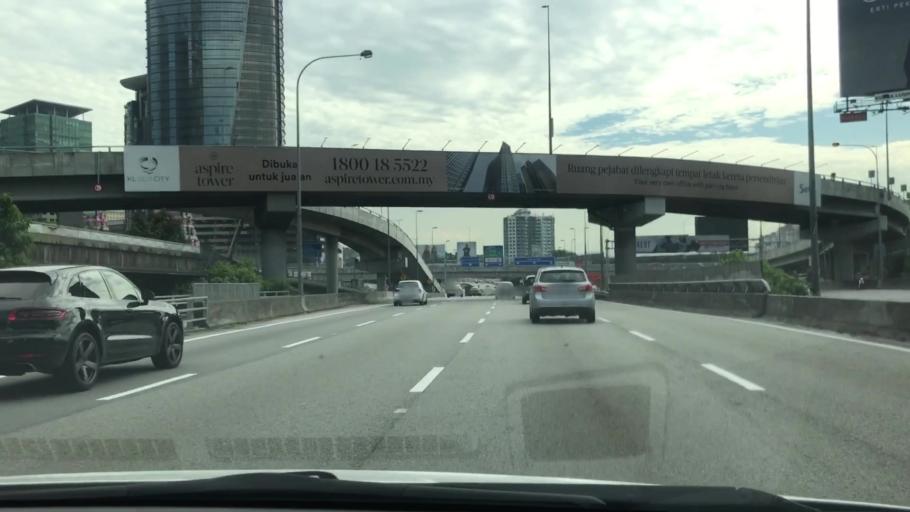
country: MY
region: Kuala Lumpur
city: Kuala Lumpur
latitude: 3.1148
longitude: 101.6723
